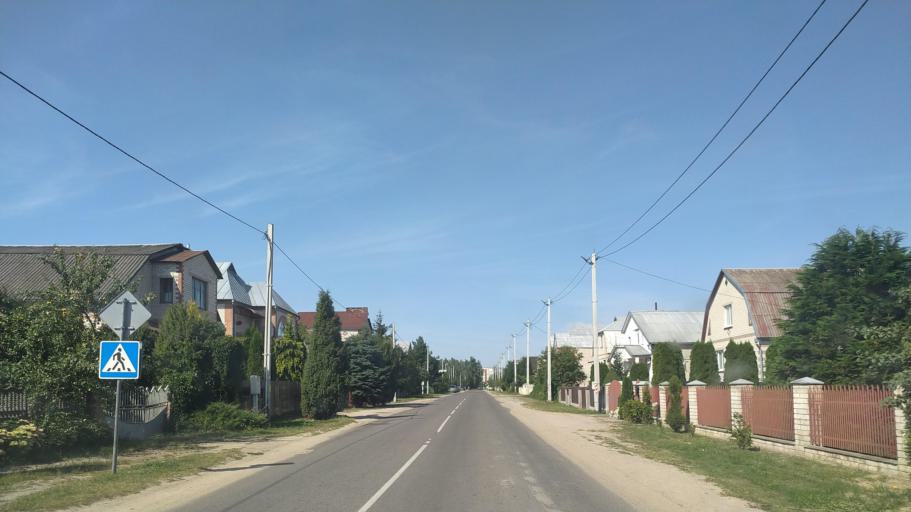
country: BY
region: Brest
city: Byaroza
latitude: 52.5313
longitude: 24.9956
